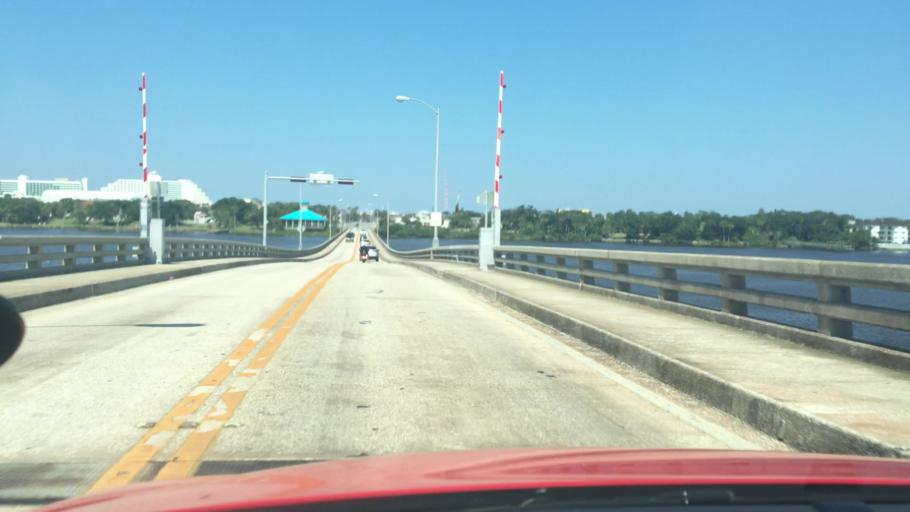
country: US
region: Florida
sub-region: Volusia County
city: Daytona Beach
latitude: 29.2233
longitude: -81.0185
